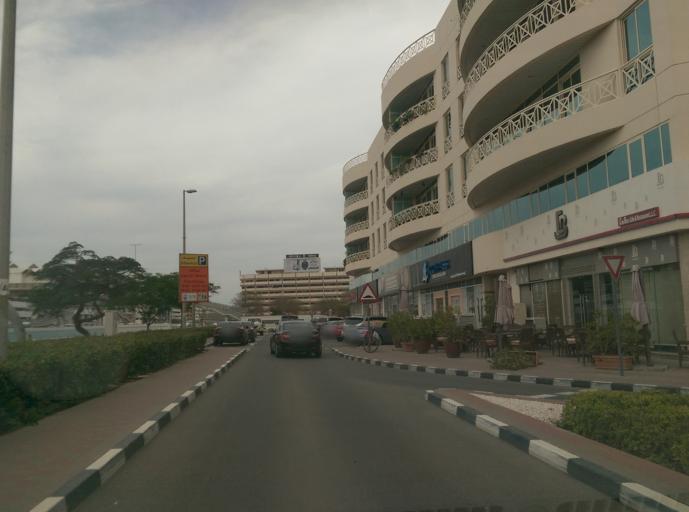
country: AE
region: Ash Shariqah
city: Sharjah
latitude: 25.2373
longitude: 55.3057
